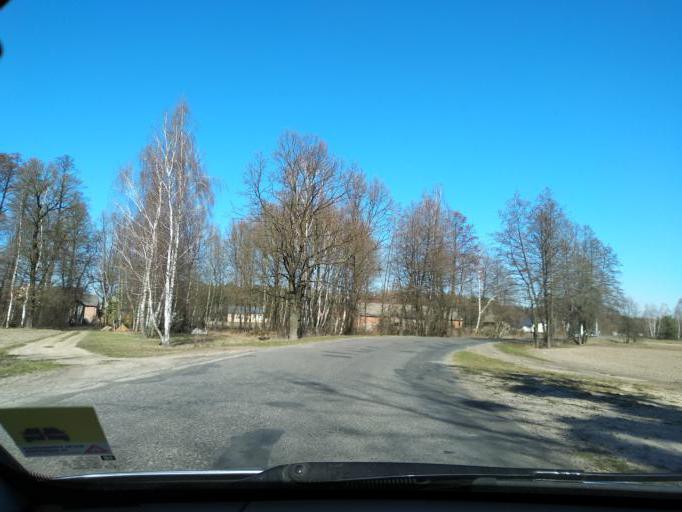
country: PL
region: Lublin Voivodeship
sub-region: Powiat pulawski
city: Kurow
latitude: 51.4235
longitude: 22.2034
